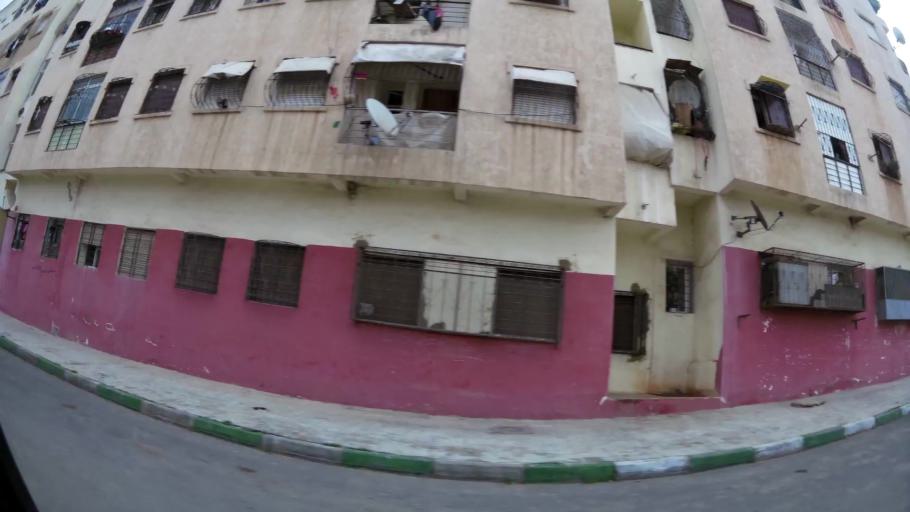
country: MA
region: Grand Casablanca
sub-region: Mediouna
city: Tit Mellil
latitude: 33.5567
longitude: -7.5316
